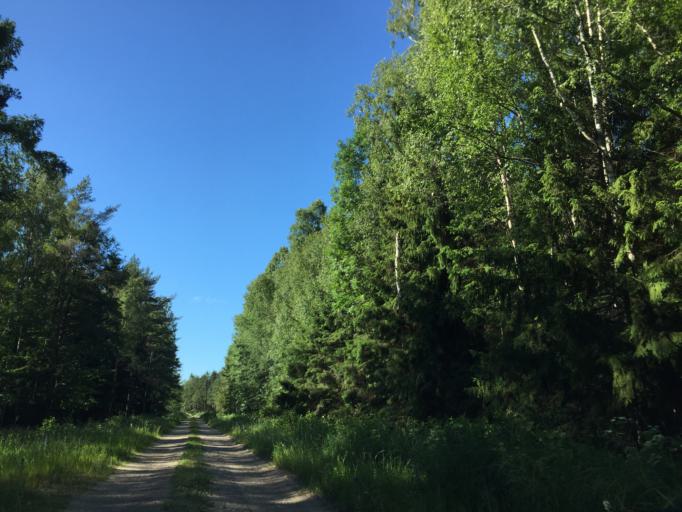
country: LV
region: Ventspils
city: Ventspils
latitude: 57.5503
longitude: 21.7639
